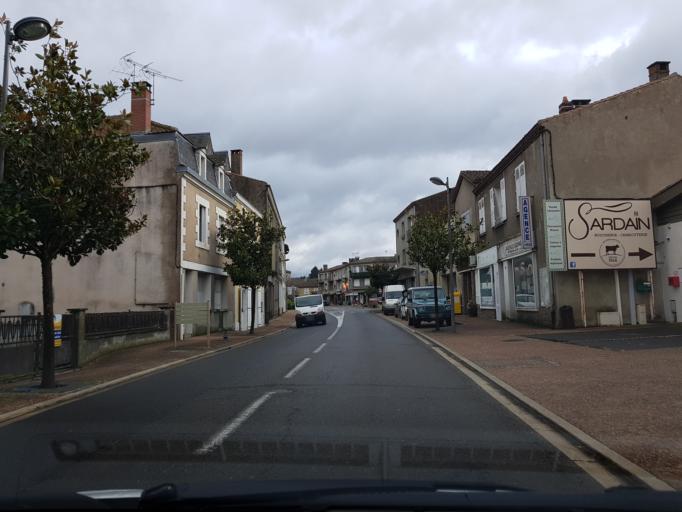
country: FR
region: Poitou-Charentes
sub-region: Departement de la Charente
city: Chabanais
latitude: 45.8735
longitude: 0.7168
